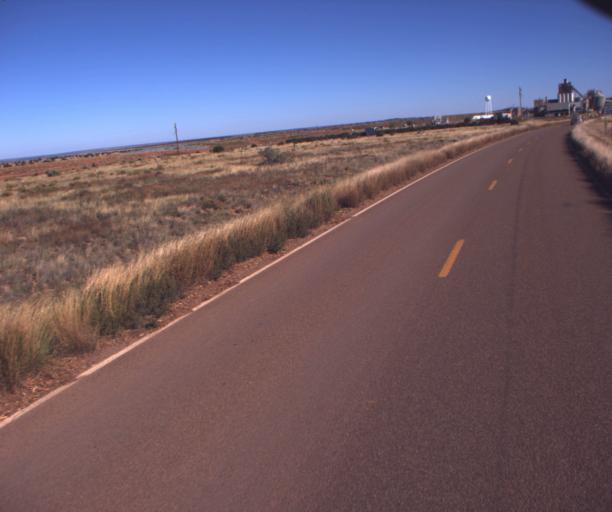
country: US
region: Arizona
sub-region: Navajo County
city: Heber-Overgaard
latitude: 34.4948
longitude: -110.3401
